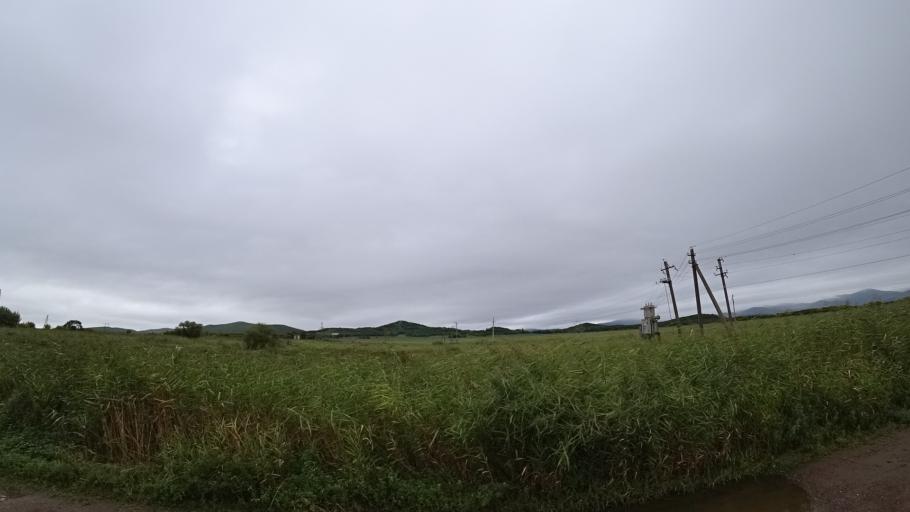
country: RU
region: Primorskiy
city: Monastyrishche
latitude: 44.2261
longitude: 132.4579
